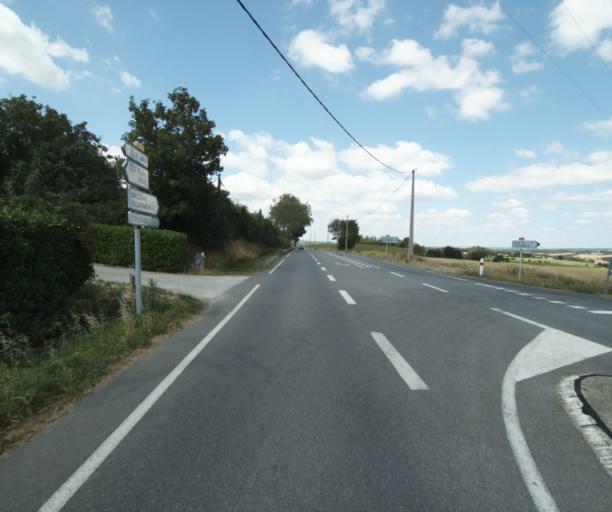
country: FR
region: Midi-Pyrenees
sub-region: Departement de la Haute-Garonne
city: Saint-Felix-Lauragais
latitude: 43.4614
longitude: 1.8341
